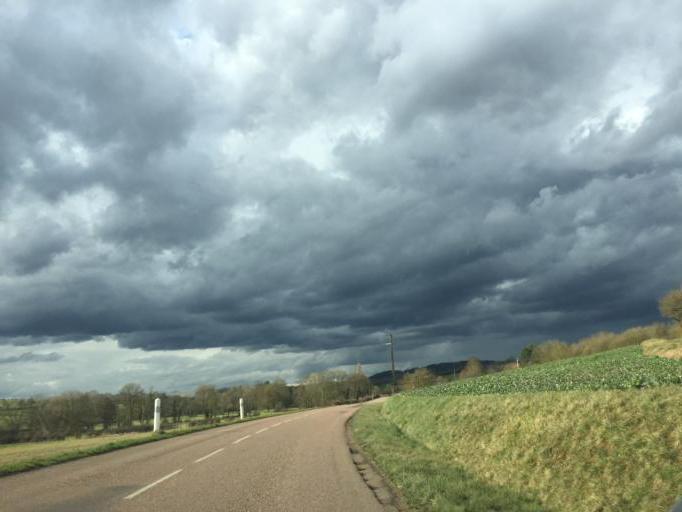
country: FR
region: Bourgogne
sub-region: Departement de la Nievre
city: Clamecy
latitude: 47.4617
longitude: 3.4550
